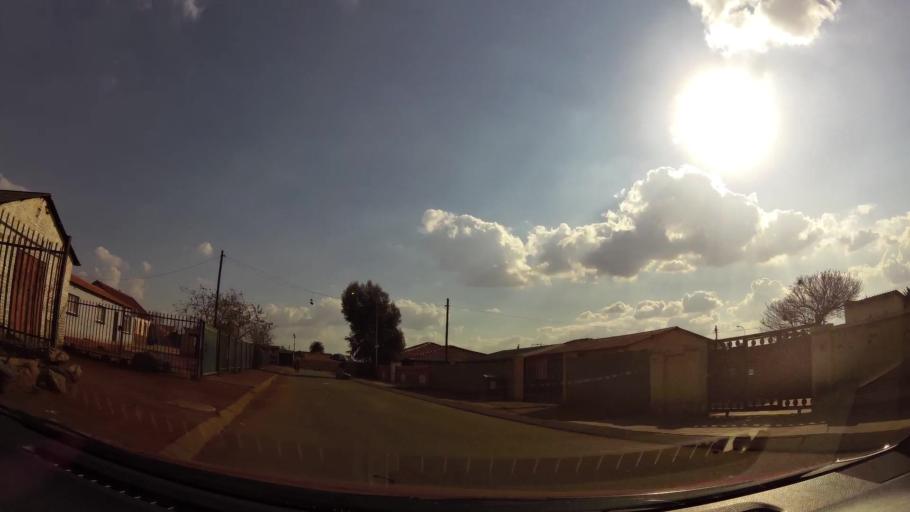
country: ZA
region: Gauteng
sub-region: City of Johannesburg Metropolitan Municipality
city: Soweto
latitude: -26.2246
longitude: 27.8710
